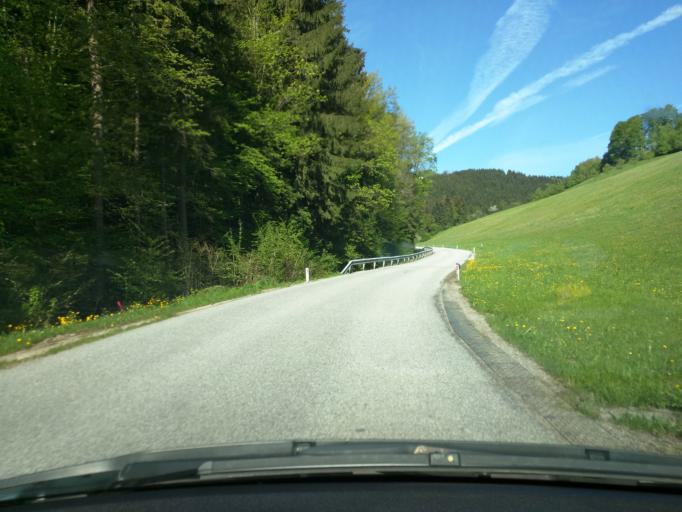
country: AT
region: Lower Austria
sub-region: Politischer Bezirk Scheibbs
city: Randegg
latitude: 48.0259
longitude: 14.9455
